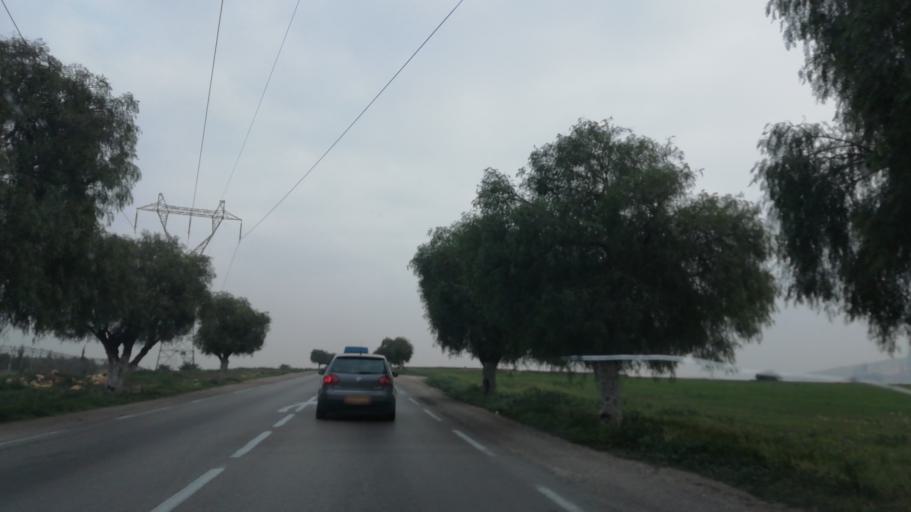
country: DZ
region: Mascara
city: Sig
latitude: 35.5455
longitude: -0.3036
